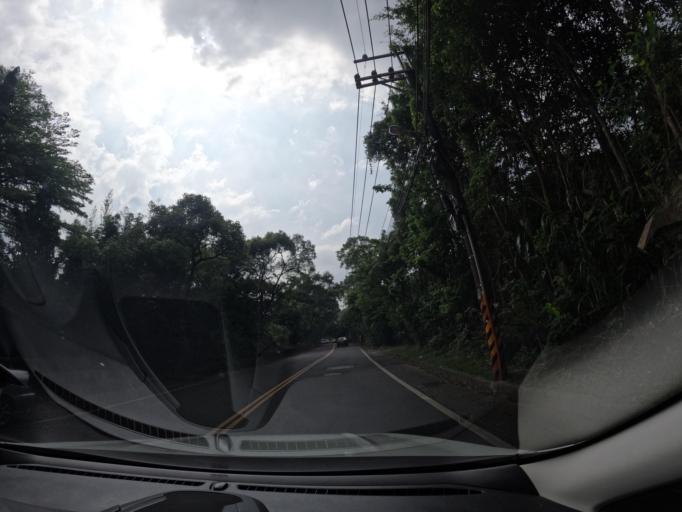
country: TW
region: Taiwan
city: Daxi
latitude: 24.9105
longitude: 121.3913
